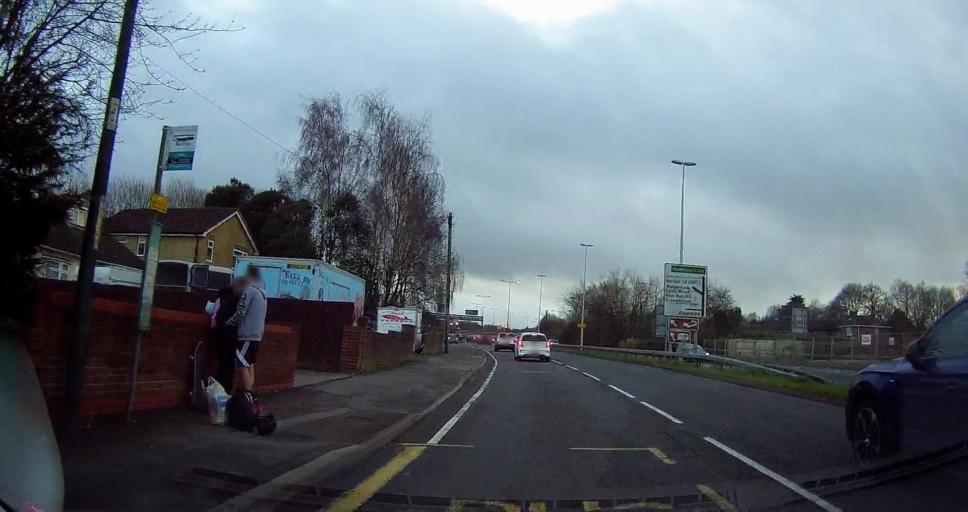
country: GB
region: England
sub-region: Kent
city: Chatham
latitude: 51.3460
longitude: 0.5075
